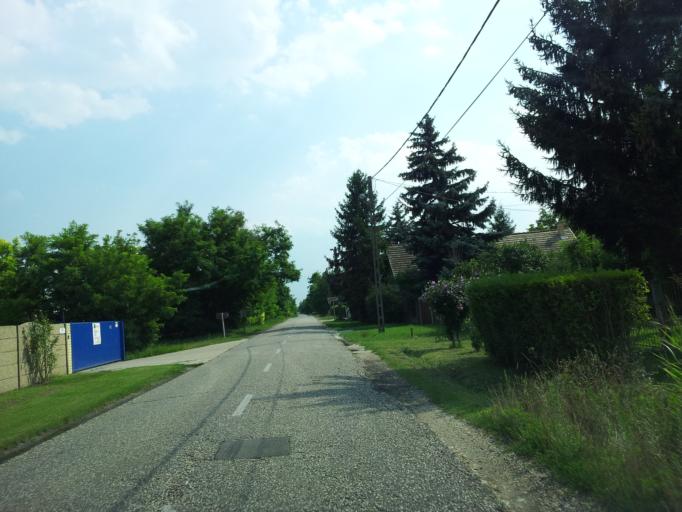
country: HU
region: Pest
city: Szigetujfalu
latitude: 47.2254
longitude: 18.9207
